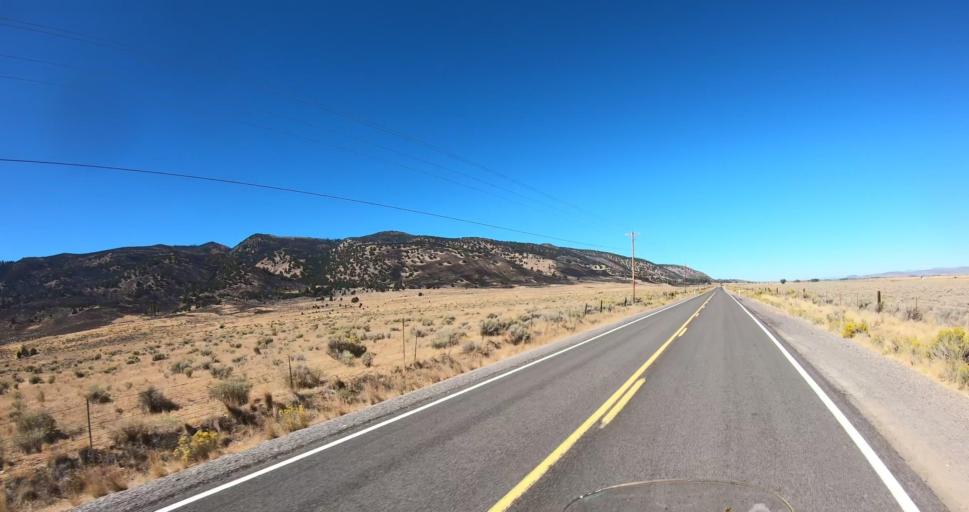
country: US
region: Oregon
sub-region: Lake County
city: Lakeview
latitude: 42.6220
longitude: -120.5062
